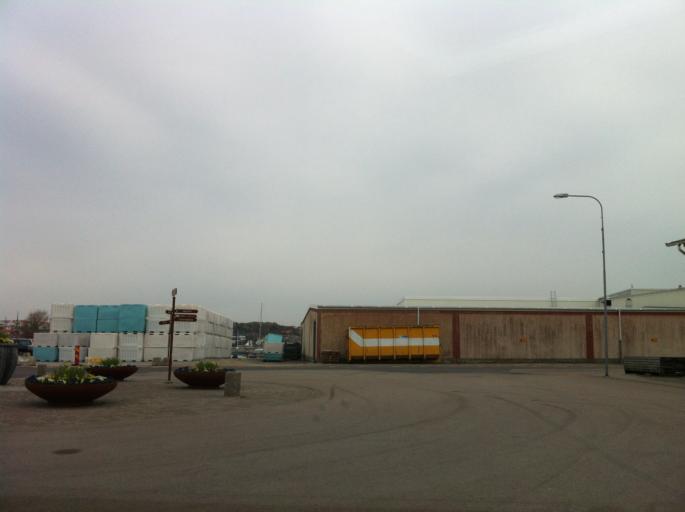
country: SE
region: Vaestra Goetaland
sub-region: Tjorns Kommun
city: Myggenas
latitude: 58.1437
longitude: 11.7096
